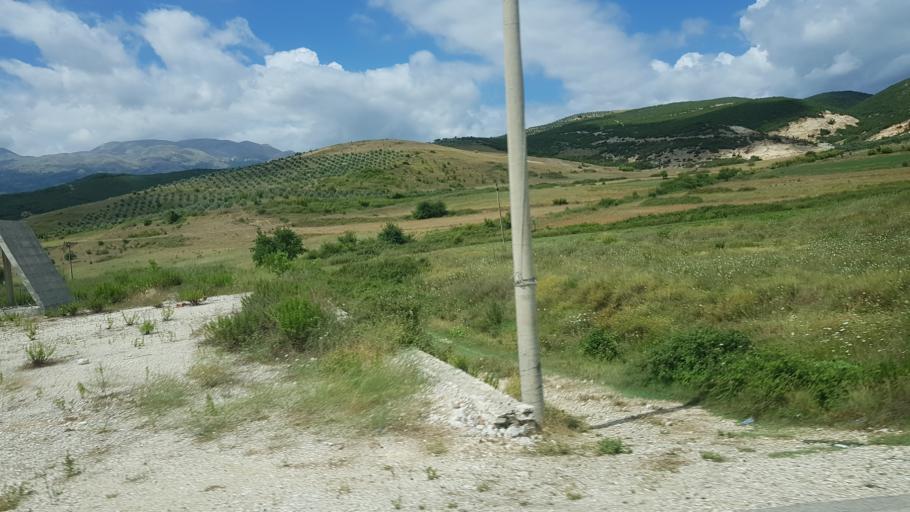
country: AL
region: Gjirokaster
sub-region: Rrethi i Tepelenes
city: Krahes
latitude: 40.4253
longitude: 19.8546
